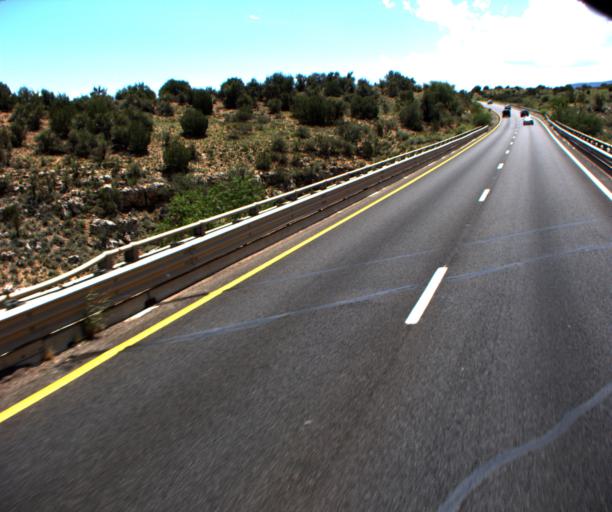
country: US
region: Arizona
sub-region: Yavapai County
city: Verde Village
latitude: 34.6690
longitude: -111.9700
